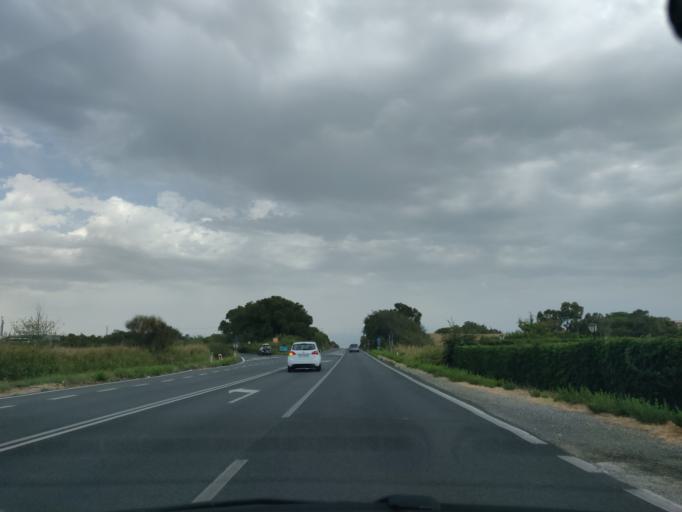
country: IT
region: Latium
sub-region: Citta metropolitana di Roma Capitale
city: Santa Marinella
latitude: 42.0318
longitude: 11.9346
